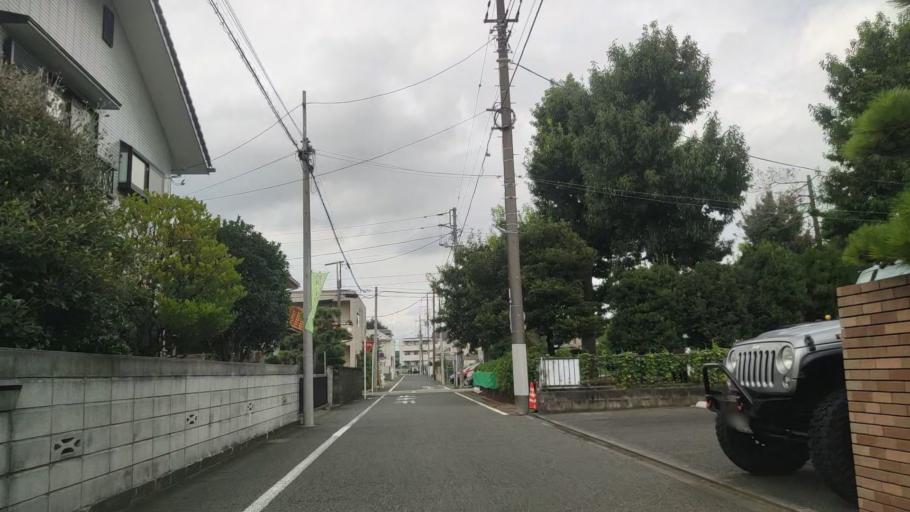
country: JP
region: Kanagawa
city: Minami-rinkan
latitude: 35.5030
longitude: 139.4424
